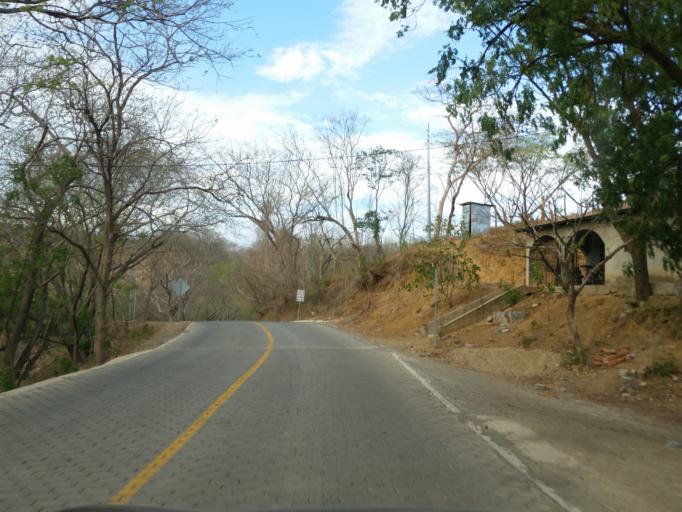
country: NI
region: Rivas
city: Tola
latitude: 11.3911
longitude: -85.9812
